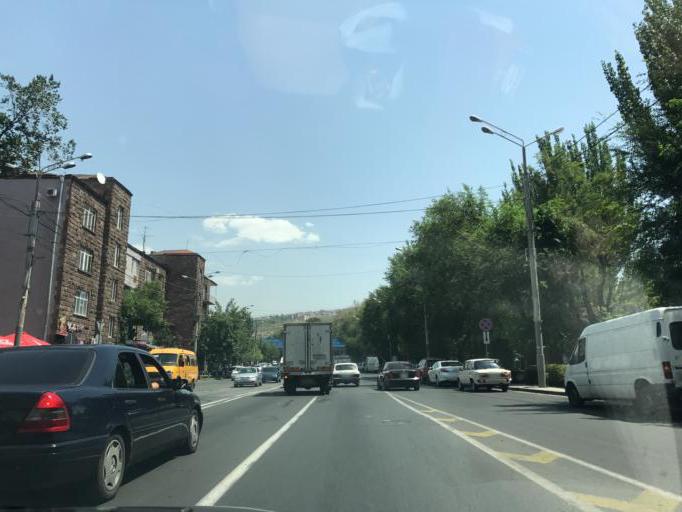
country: AM
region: Yerevan
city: Yerevan
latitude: 40.1734
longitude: 44.5155
